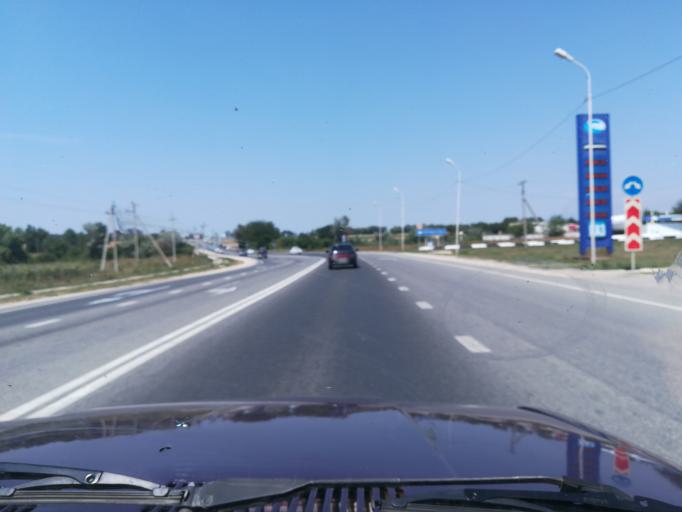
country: RU
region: Krasnodarskiy
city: Tsibanobalka
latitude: 44.9776
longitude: 37.3220
